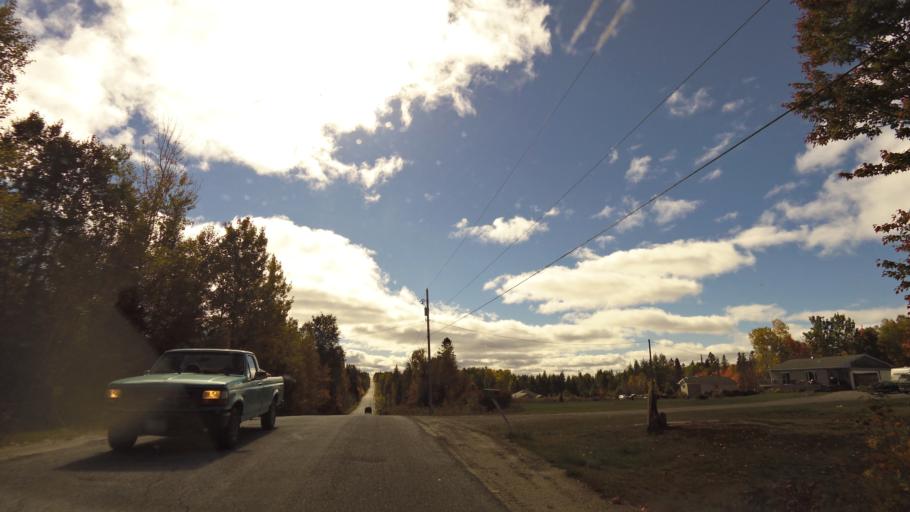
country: CA
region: Ontario
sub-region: Nipissing District
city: North Bay
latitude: 46.3695
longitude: -79.4872
